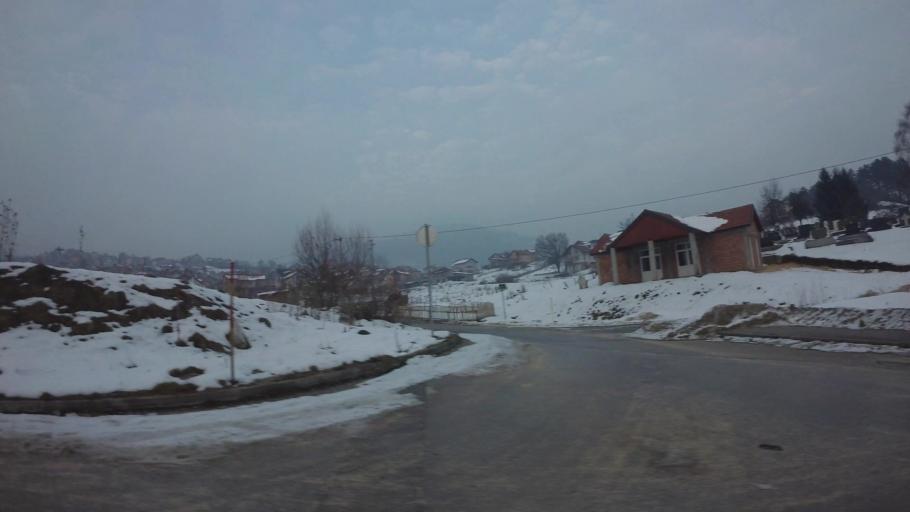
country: BA
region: Federation of Bosnia and Herzegovina
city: Vogosca
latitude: 43.9012
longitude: 18.3549
